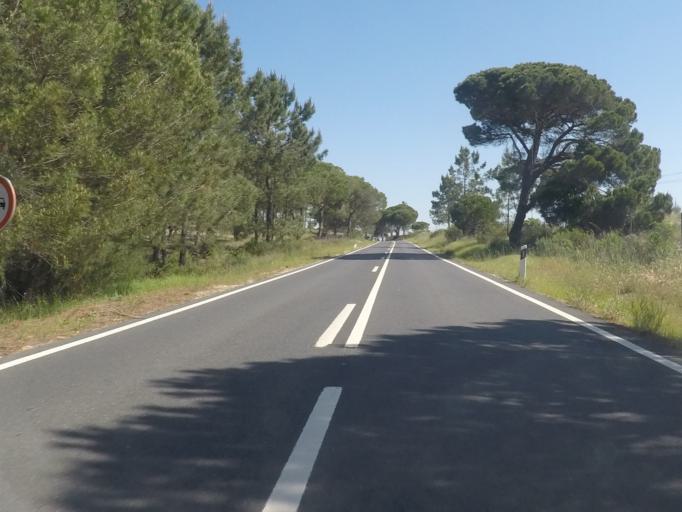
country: PT
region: Setubal
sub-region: Grandola
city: Grandola
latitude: 38.2773
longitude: -8.7261
